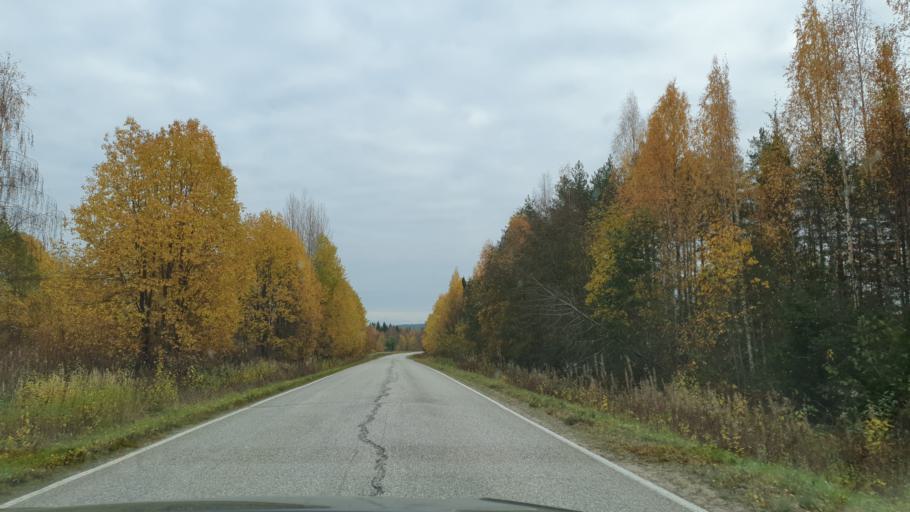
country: FI
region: Kainuu
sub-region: Kajaani
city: Ristijaervi
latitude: 64.4689
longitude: 28.3014
